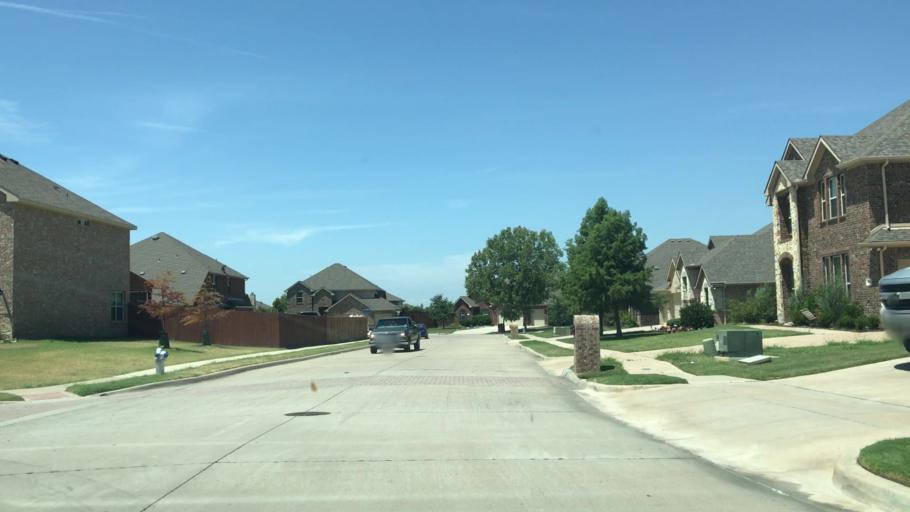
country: US
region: Texas
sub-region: Collin County
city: Saint Paul
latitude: 33.0282
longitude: -96.5484
